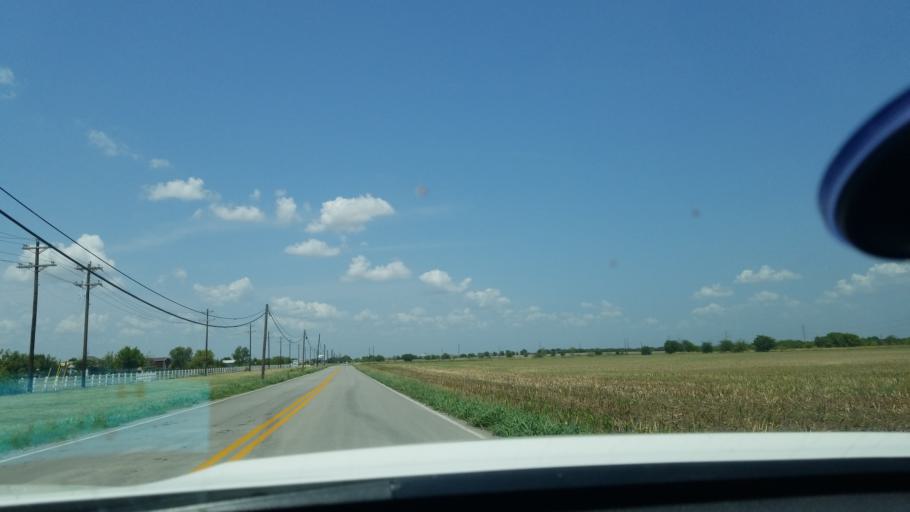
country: US
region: Texas
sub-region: Tarrant County
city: Eagle Mountain
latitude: 32.9403
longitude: -97.4094
